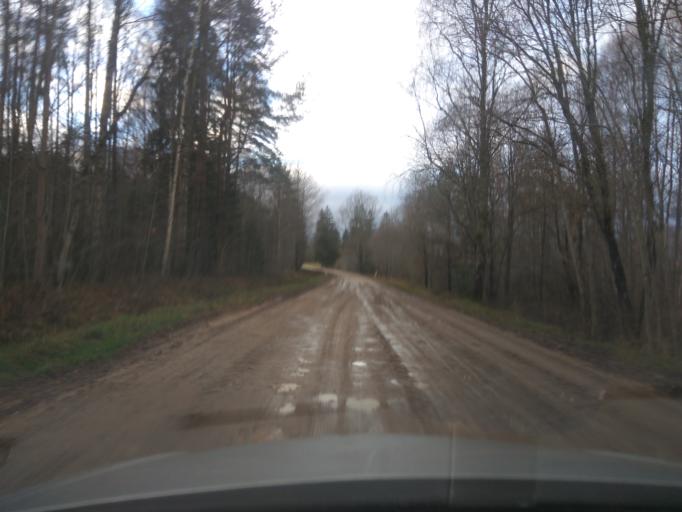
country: LV
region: Kuldigas Rajons
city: Kuldiga
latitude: 56.8340
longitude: 21.8161
